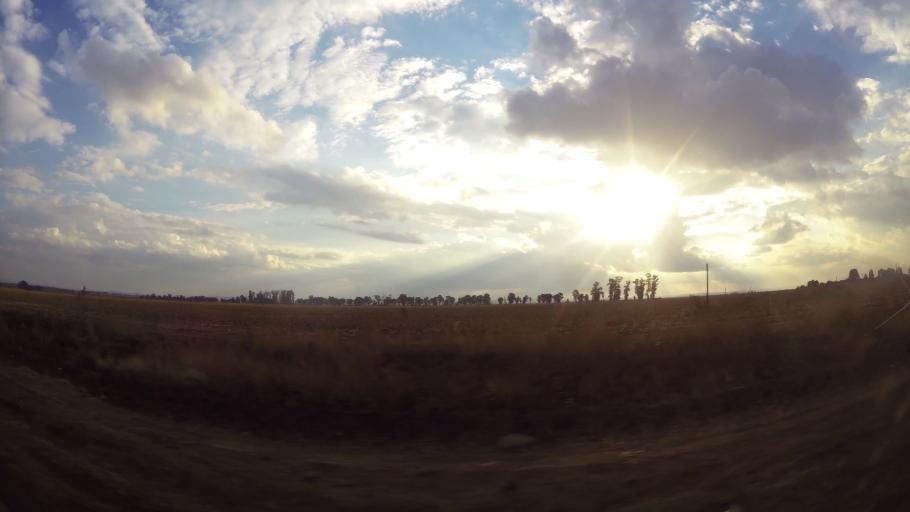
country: ZA
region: Gauteng
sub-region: Sedibeng District Municipality
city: Vanderbijlpark
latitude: -26.6492
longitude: 27.8036
